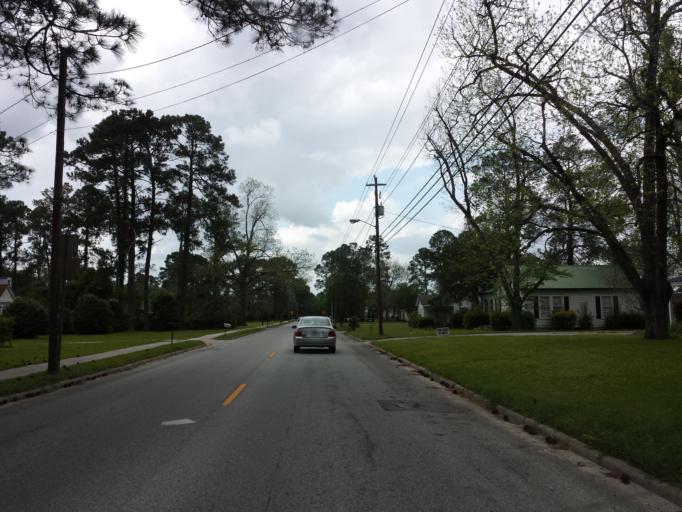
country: US
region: Georgia
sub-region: Lowndes County
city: Hahira
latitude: 30.9952
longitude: -83.3740
